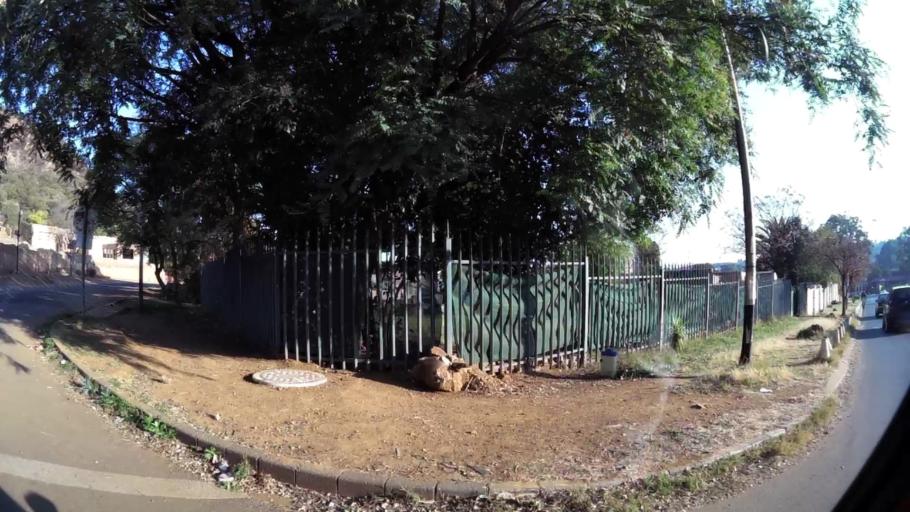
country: ZA
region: Gauteng
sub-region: City of Johannesburg Metropolitan Municipality
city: Soweto
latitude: -26.2772
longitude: 27.9606
